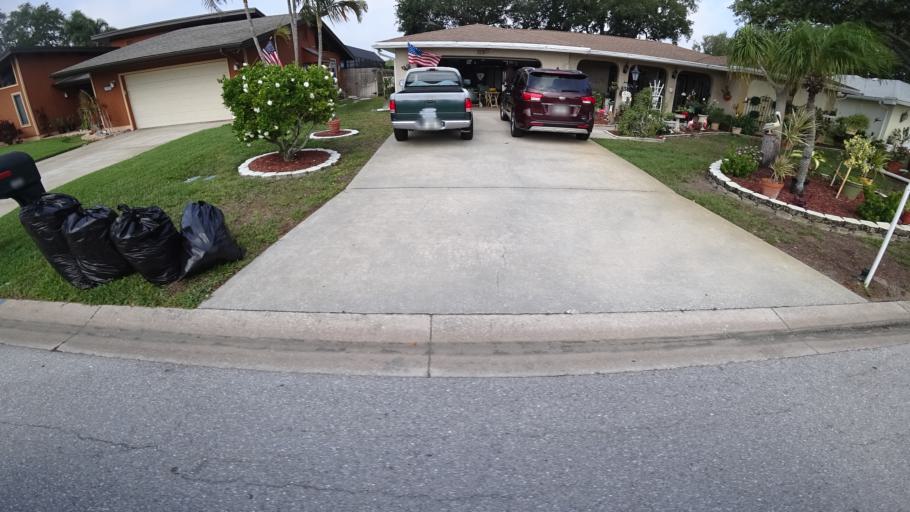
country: US
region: Florida
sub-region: Manatee County
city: West Bradenton
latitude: 27.4860
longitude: -82.6159
